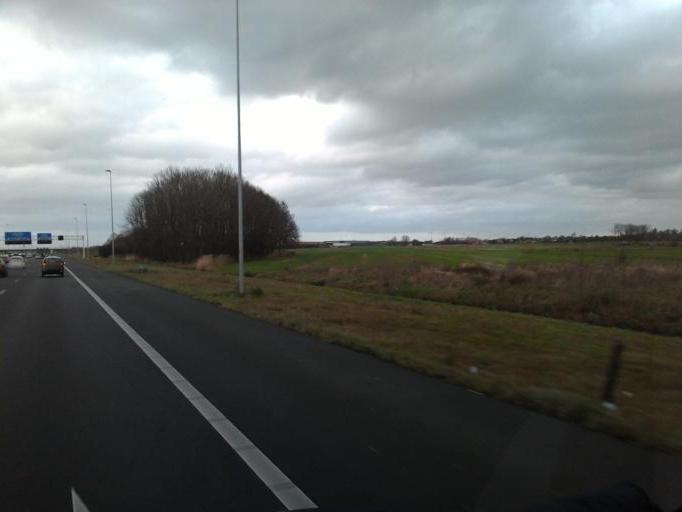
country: NL
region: Utrecht
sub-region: Gemeente Vianen
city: Vianen
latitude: 51.9678
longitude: 5.1117
